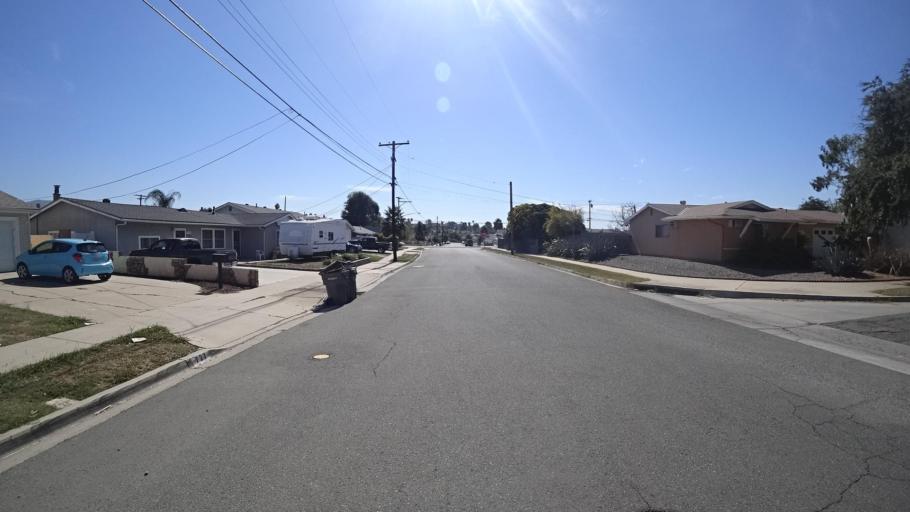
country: US
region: California
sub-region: San Diego County
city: La Presa
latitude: 32.7100
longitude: -117.0044
